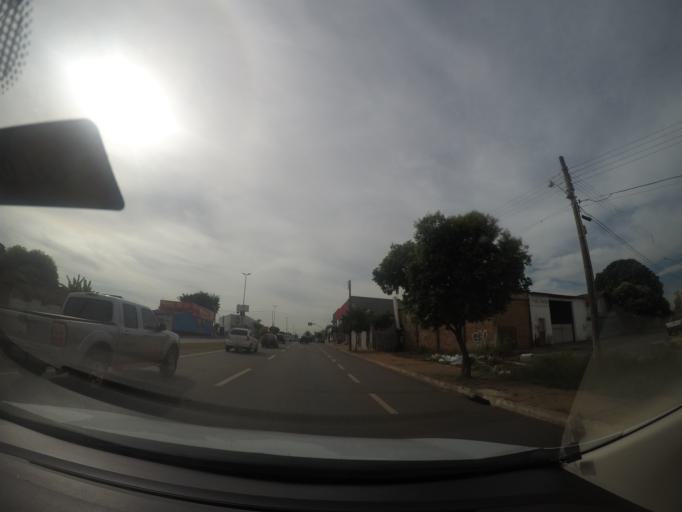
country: BR
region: Goias
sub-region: Goiania
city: Goiania
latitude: -16.6593
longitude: -49.2935
